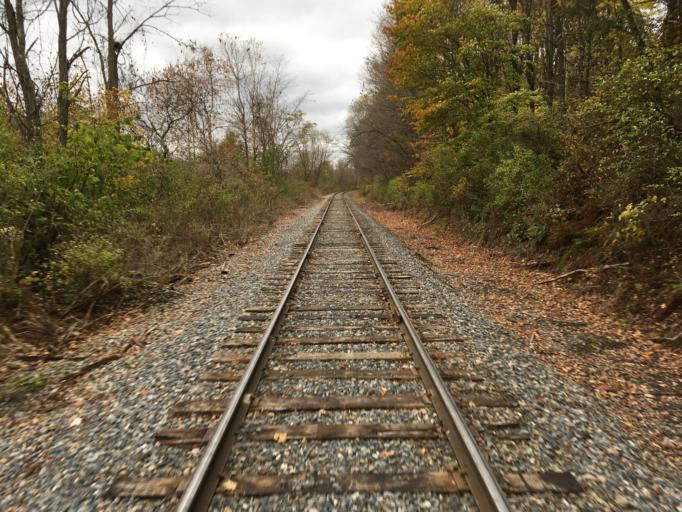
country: US
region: New Hampshire
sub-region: Grafton County
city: Woodsville
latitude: 44.1802
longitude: -72.0589
